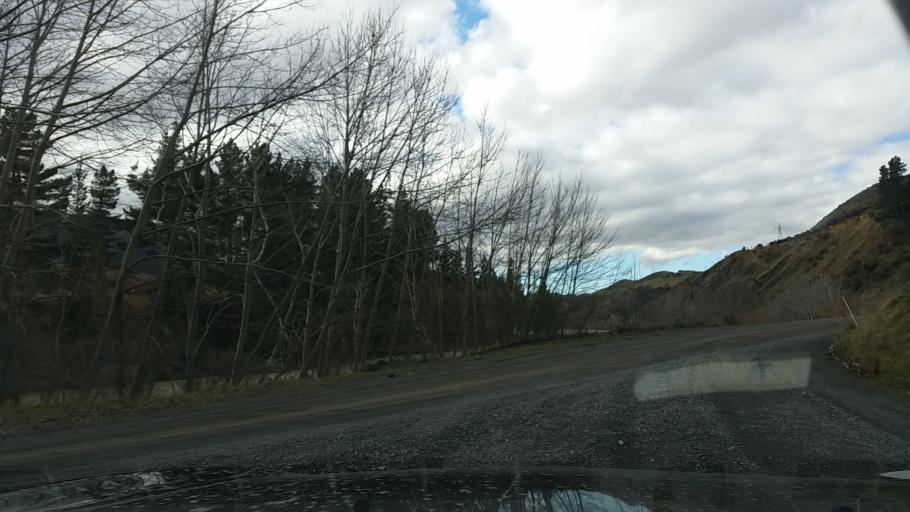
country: NZ
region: Canterbury
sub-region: Kaikoura District
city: Kaikoura
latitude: -41.8968
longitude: 173.5985
